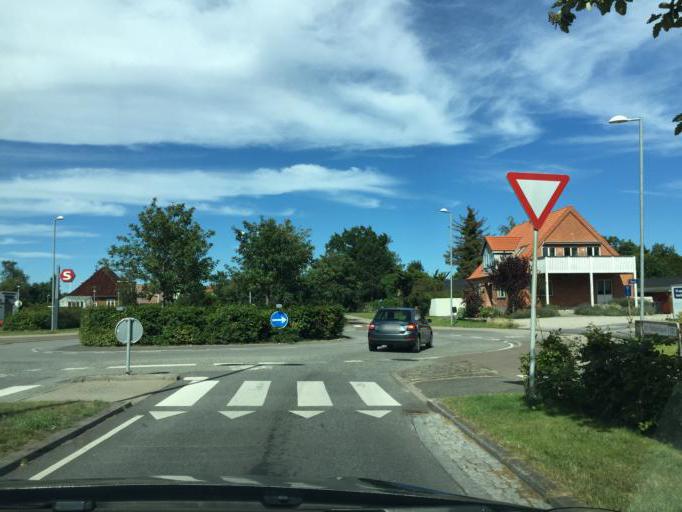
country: DK
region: Zealand
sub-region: Solrod Kommune
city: Solrod Strand
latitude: 55.5336
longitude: 12.2237
